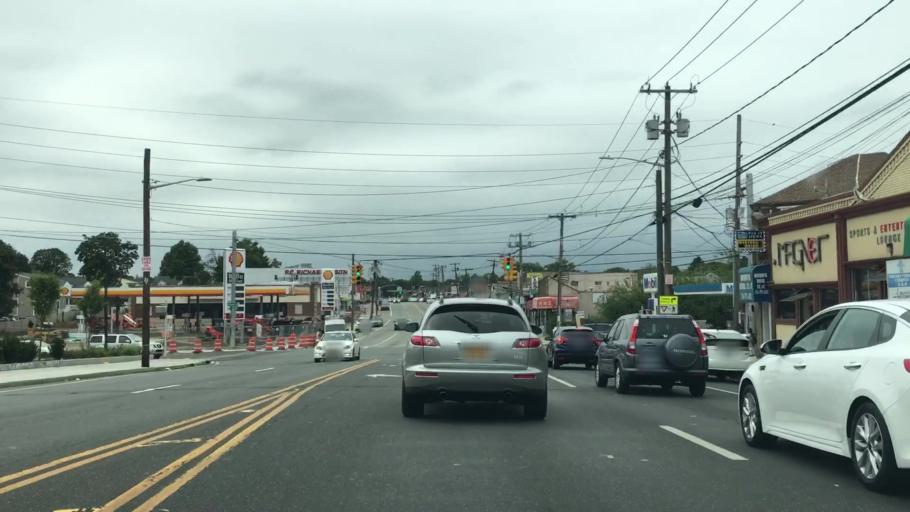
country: US
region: New York
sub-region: Nassau County
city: Elmont
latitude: 40.6892
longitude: -73.7210
